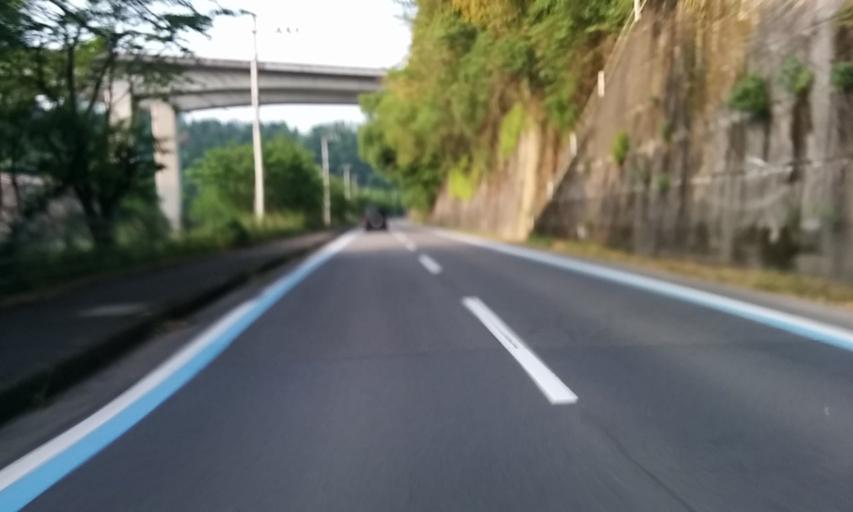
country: JP
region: Ehime
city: Saijo
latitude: 33.8838
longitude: 133.1809
